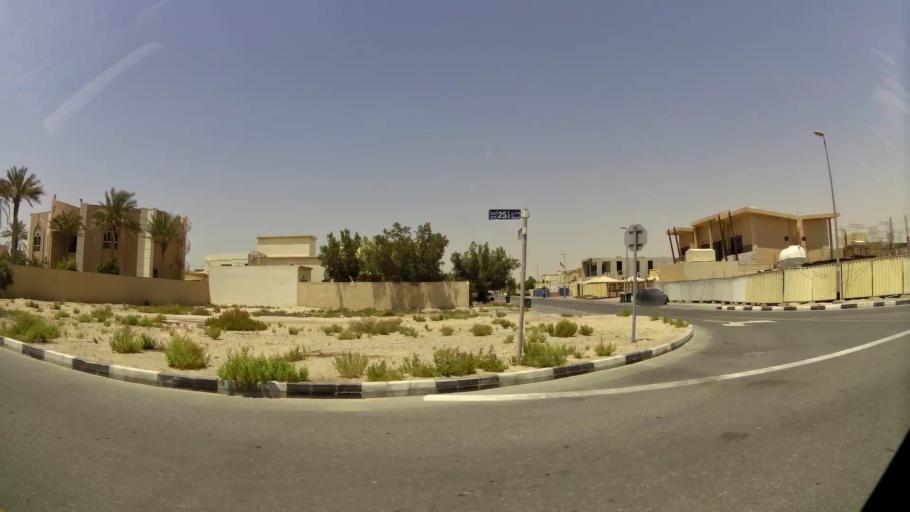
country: AE
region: Dubai
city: Dubai
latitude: 25.0845
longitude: 55.2102
